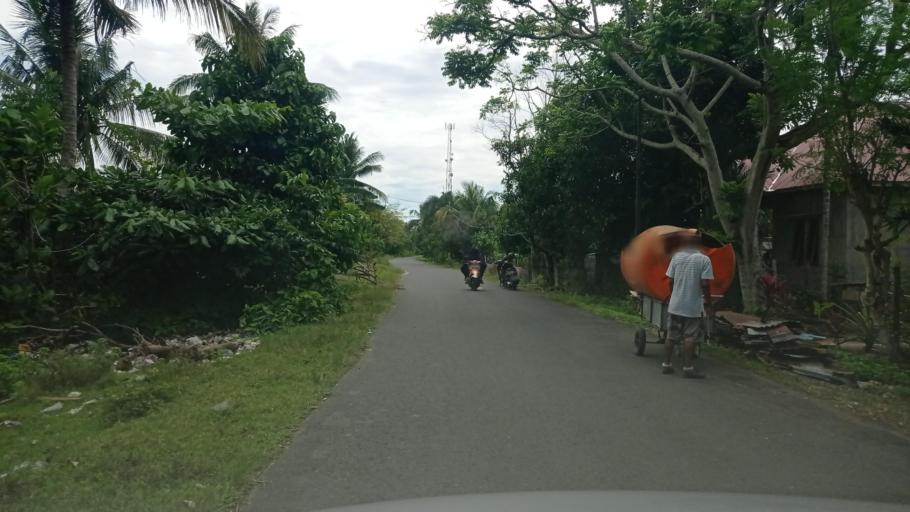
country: ID
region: Bengkulu
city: Ipuh
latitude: -2.5829
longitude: 101.1181
